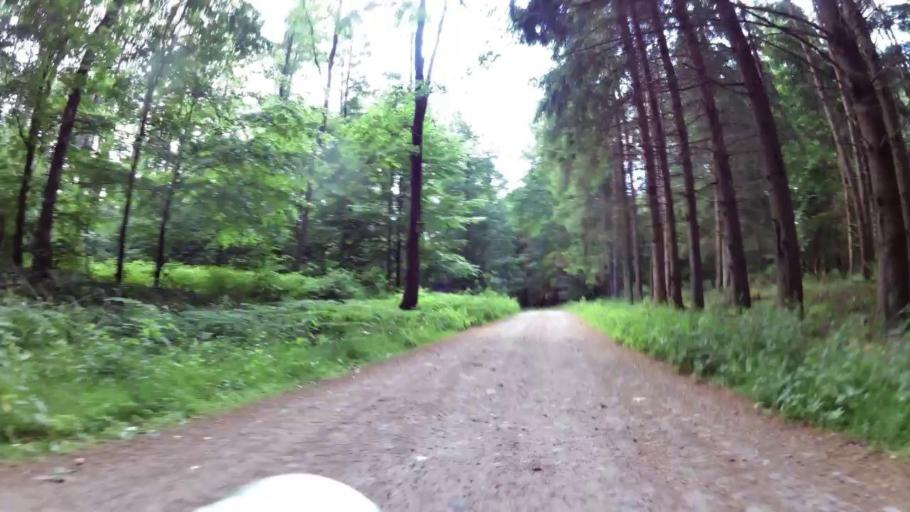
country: PL
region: West Pomeranian Voivodeship
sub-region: Powiat koszalinski
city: Bobolice
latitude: 53.9456
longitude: 16.6556
